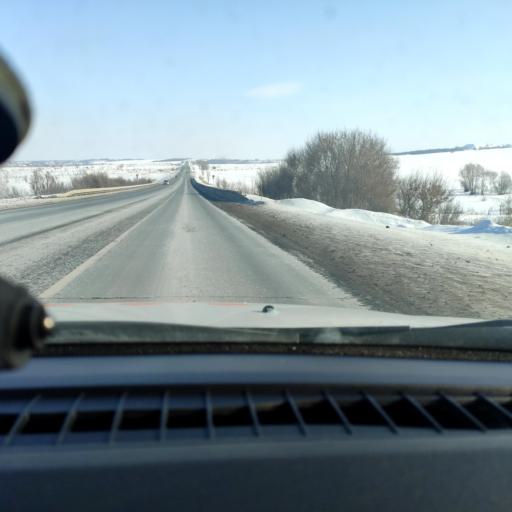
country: RU
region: Samara
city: Novosemeykino
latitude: 53.4052
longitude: 50.3762
